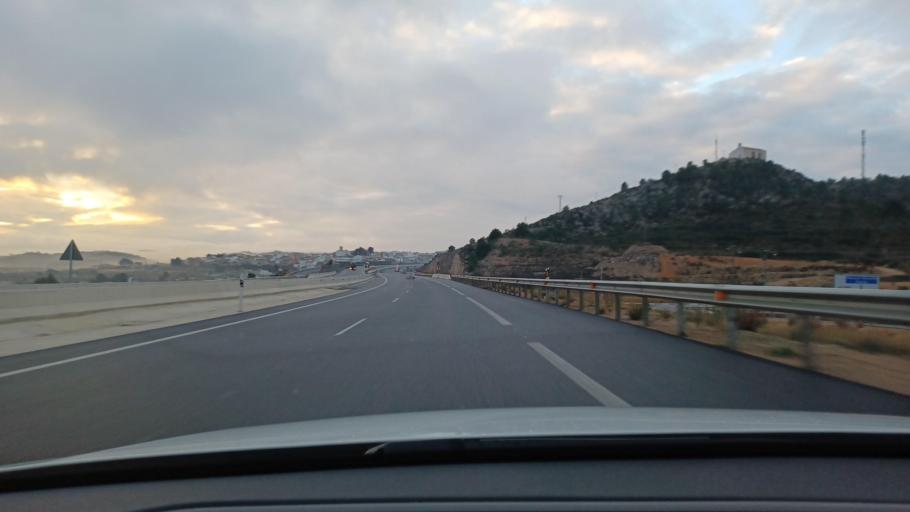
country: ES
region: Valencia
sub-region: Provincia de Valencia
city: La Font de la Figuera
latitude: 38.8171
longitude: -0.8895
